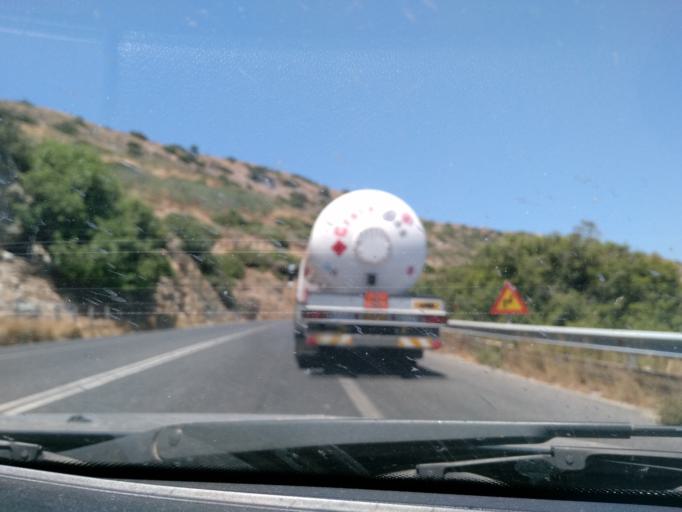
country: GR
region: Crete
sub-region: Nomos Irakleiou
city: Gazi
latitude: 35.3783
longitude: 25.0355
